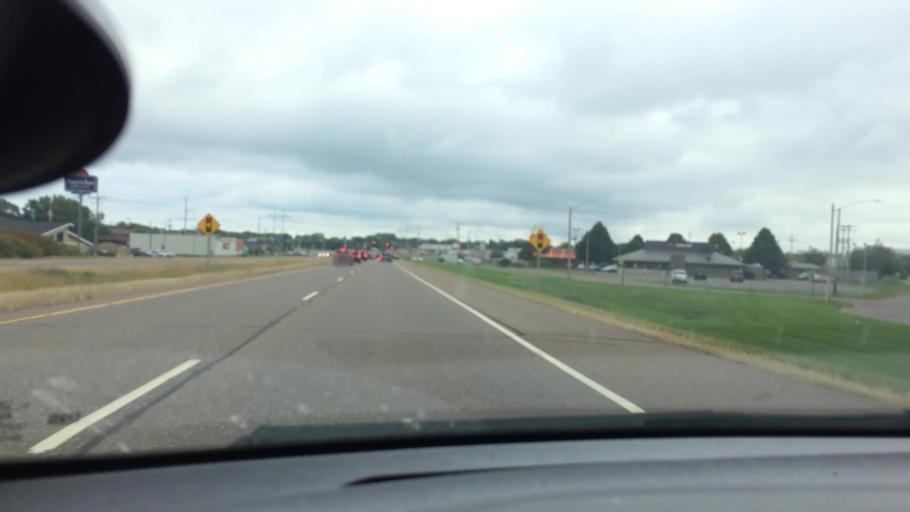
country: US
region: Wisconsin
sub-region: Chippewa County
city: Chippewa Falls
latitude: 44.9138
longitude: -91.3926
